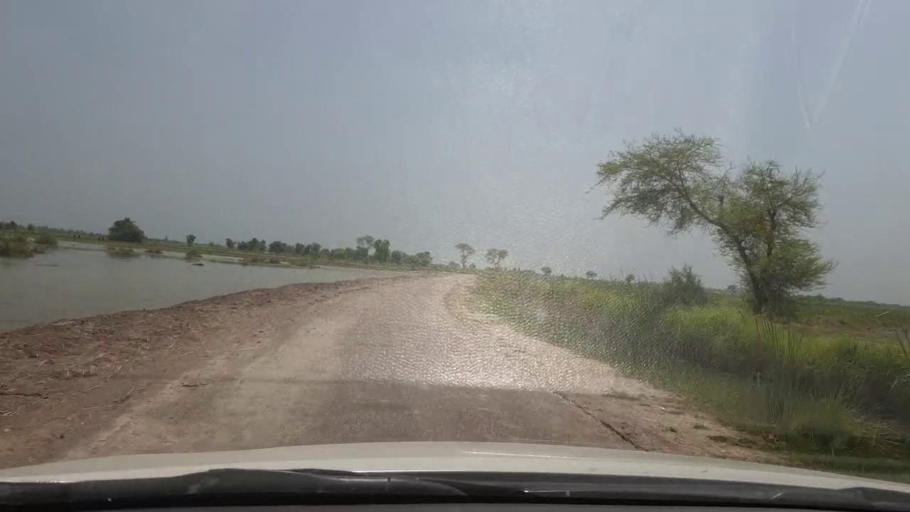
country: PK
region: Sindh
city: Shikarpur
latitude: 28.0913
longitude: 68.6204
